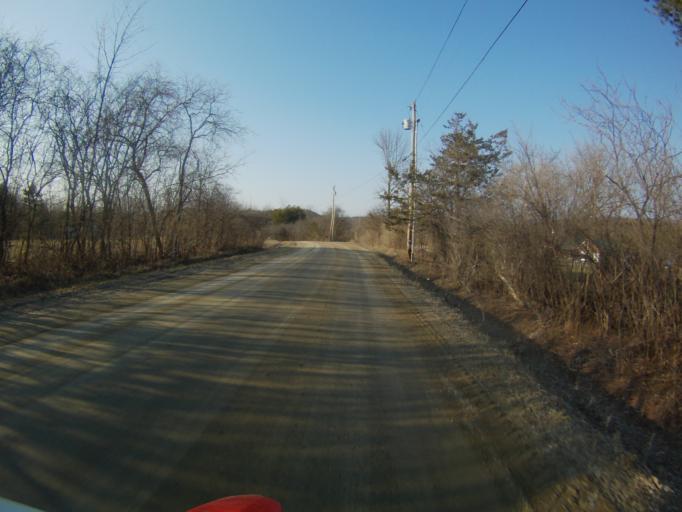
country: US
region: Vermont
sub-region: Addison County
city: Middlebury (village)
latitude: 44.0571
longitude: -73.1461
